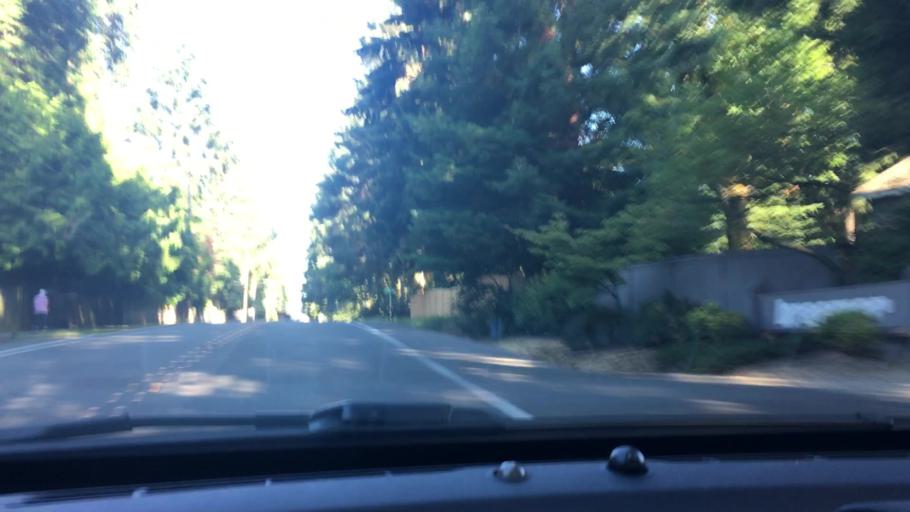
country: US
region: Washington
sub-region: King County
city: Sammamish
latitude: 47.6218
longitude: -122.1134
